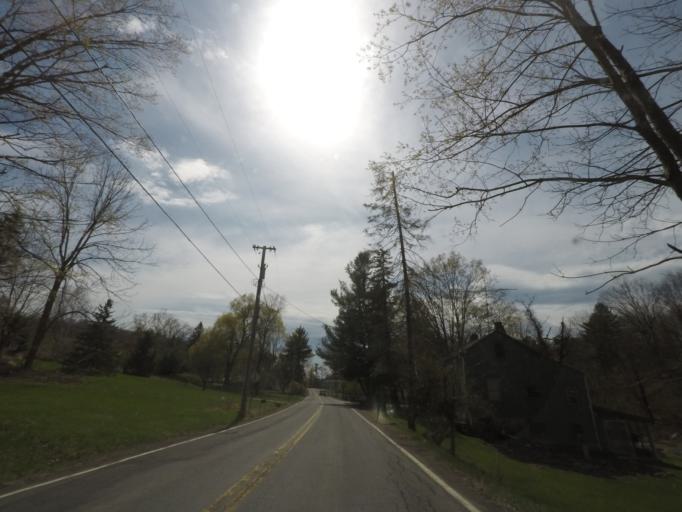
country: US
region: New York
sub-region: Columbia County
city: Chatham
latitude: 42.3417
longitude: -73.5952
